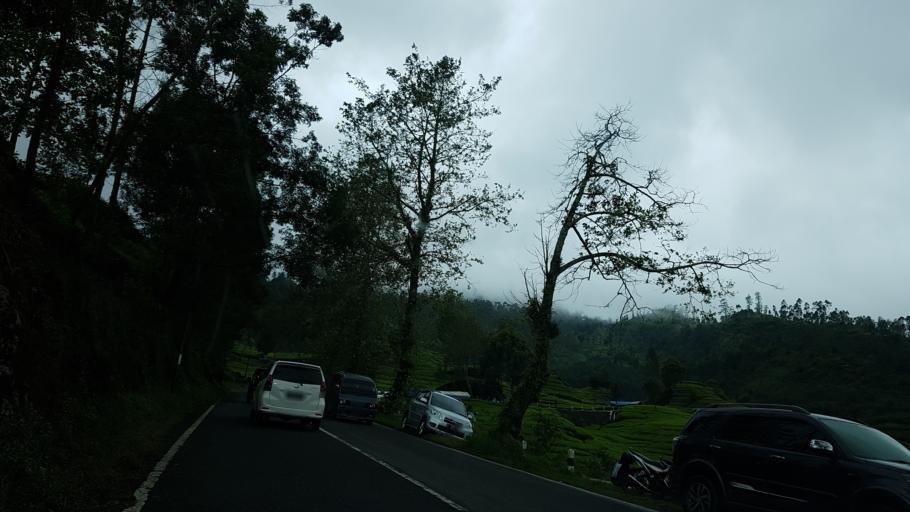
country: ID
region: West Java
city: Banjar
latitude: -7.1507
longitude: 107.3795
